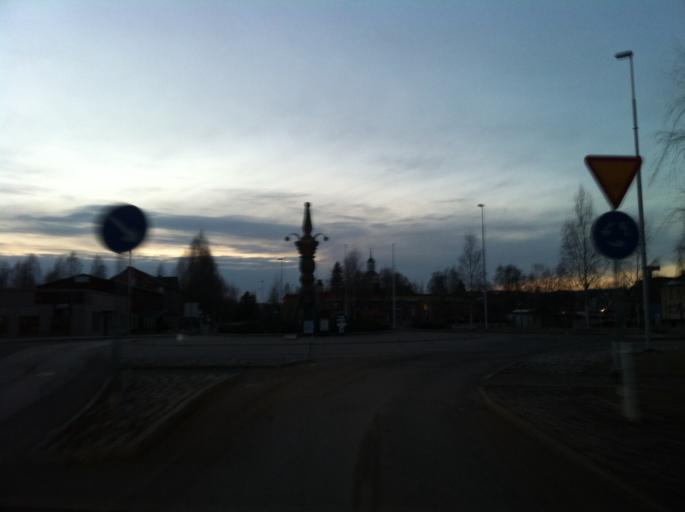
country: SE
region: Dalarna
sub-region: Orsa Kommun
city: Orsa
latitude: 61.1168
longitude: 14.6219
